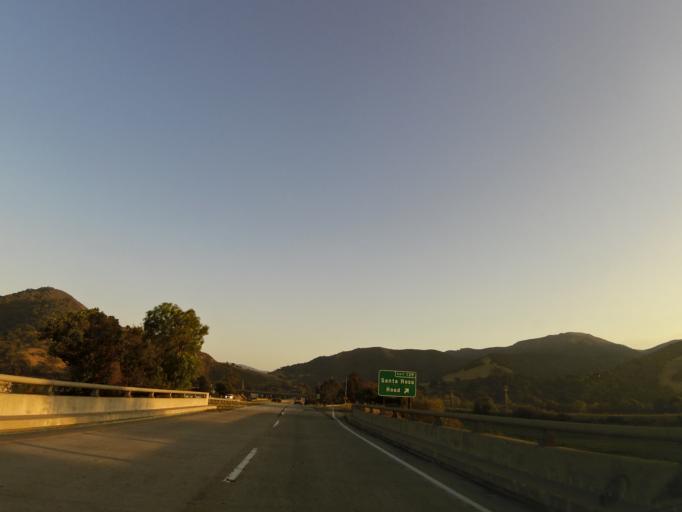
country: US
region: California
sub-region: Santa Barbara County
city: Buellton
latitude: 34.6057
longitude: -120.1915
